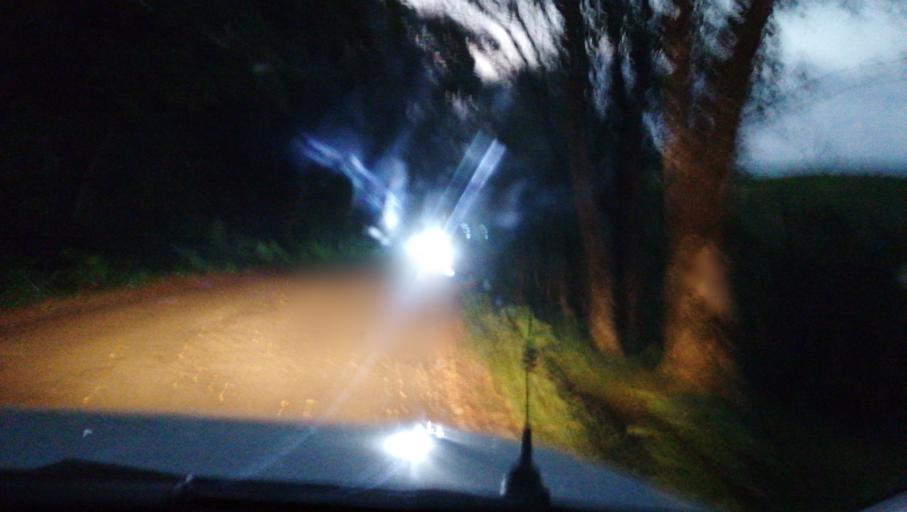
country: MX
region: Chiapas
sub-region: Ostuacan
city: Nuevo Juan del Grijalva
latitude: 17.4800
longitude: -93.3481
